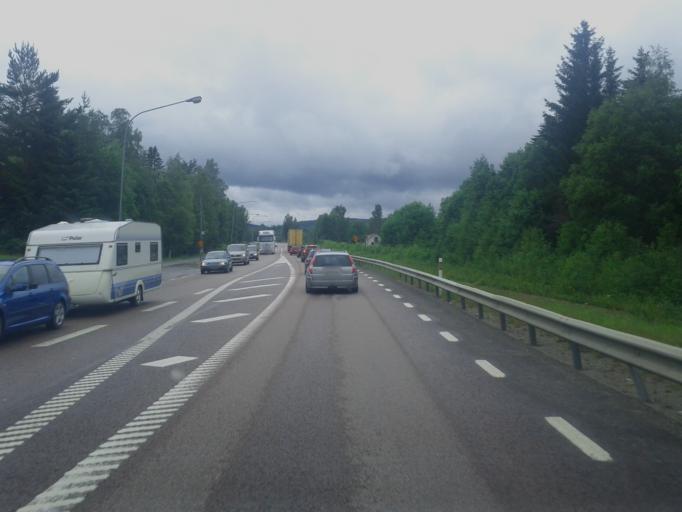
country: SE
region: Vaesternorrland
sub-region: Haernoesands Kommun
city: Haernoesand
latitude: 62.6631
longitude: 17.8537
